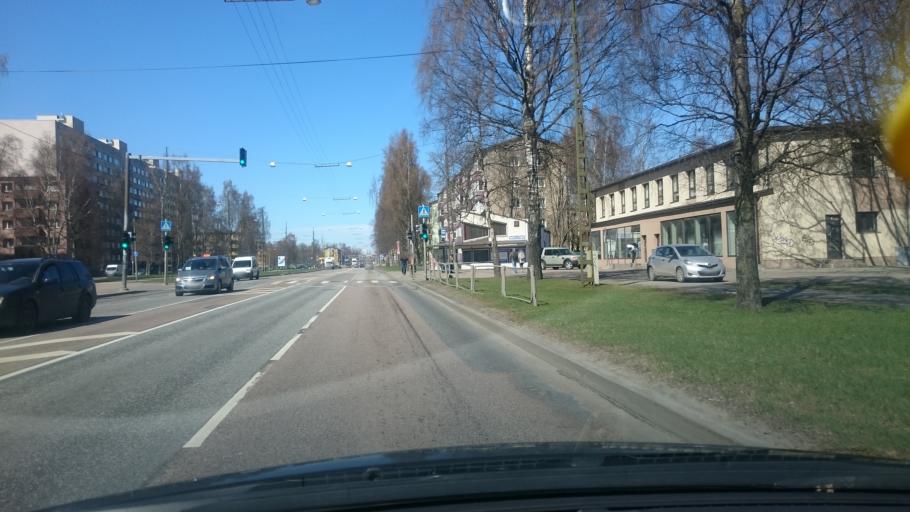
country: EE
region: Harju
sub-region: Tallinna linn
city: Tallinn
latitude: 59.4427
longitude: 24.7048
